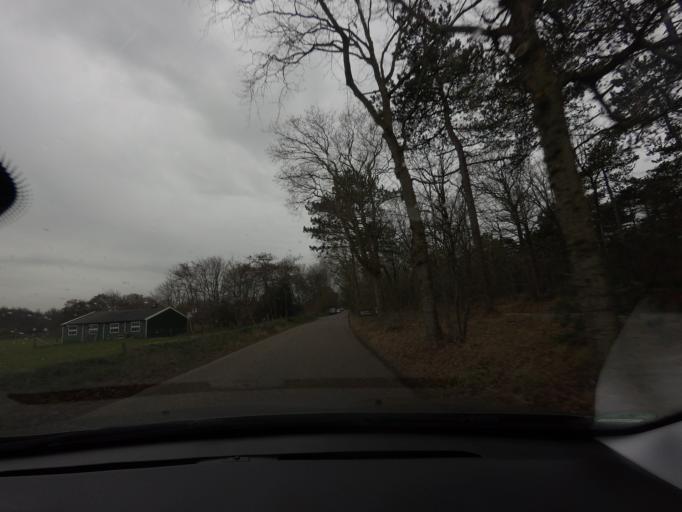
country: NL
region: North Holland
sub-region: Gemeente Texel
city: Den Burg
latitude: 53.0902
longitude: 4.7574
